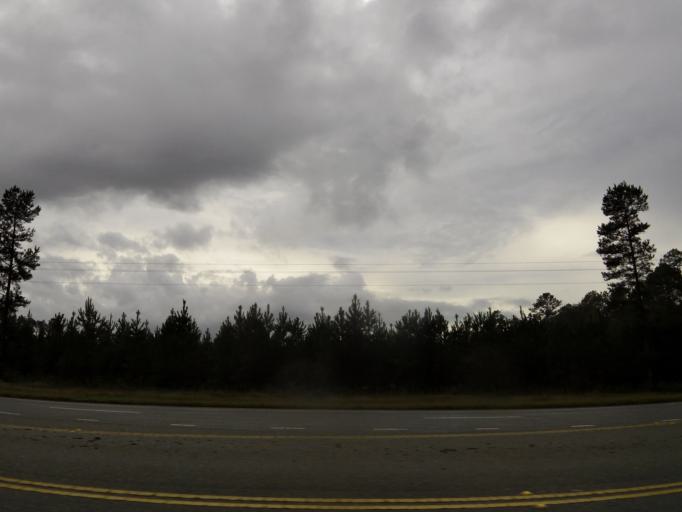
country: US
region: Georgia
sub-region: Wayne County
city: Jesup
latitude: 31.5484
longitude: -81.8102
